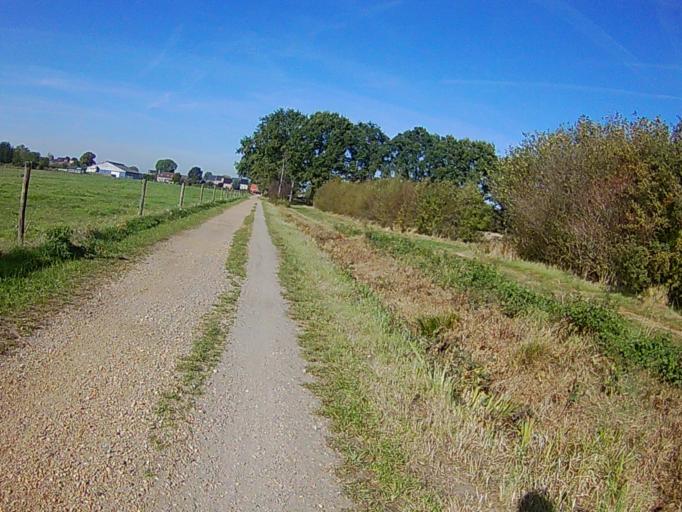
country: BE
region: Flanders
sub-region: Provincie Antwerpen
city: Stabroek
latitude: 51.3364
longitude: 4.3854
